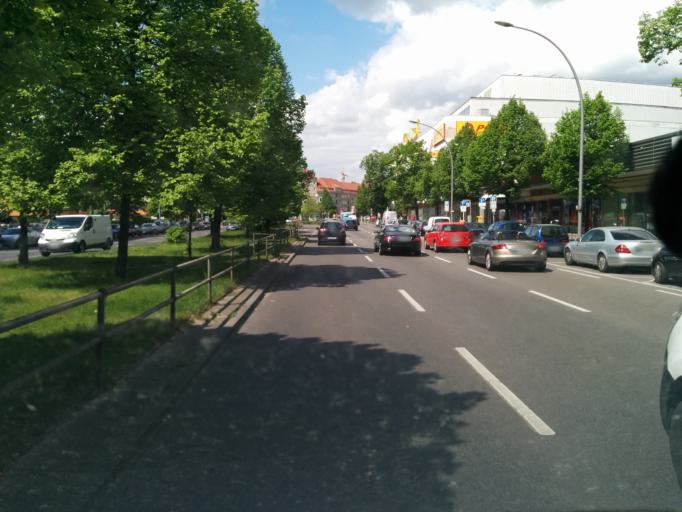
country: DE
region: Berlin
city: Siemensstadt
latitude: 52.5357
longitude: 13.2754
